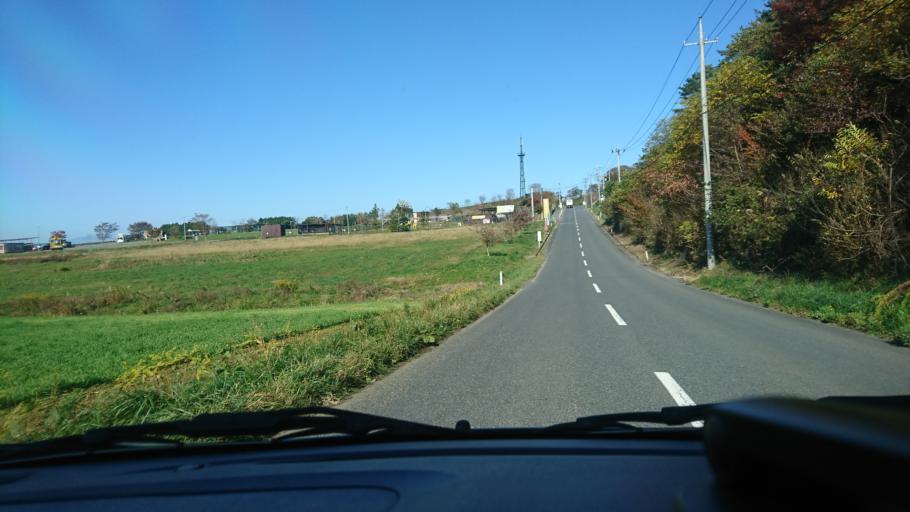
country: JP
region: Iwate
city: Ichinoseki
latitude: 38.8081
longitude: 141.2617
